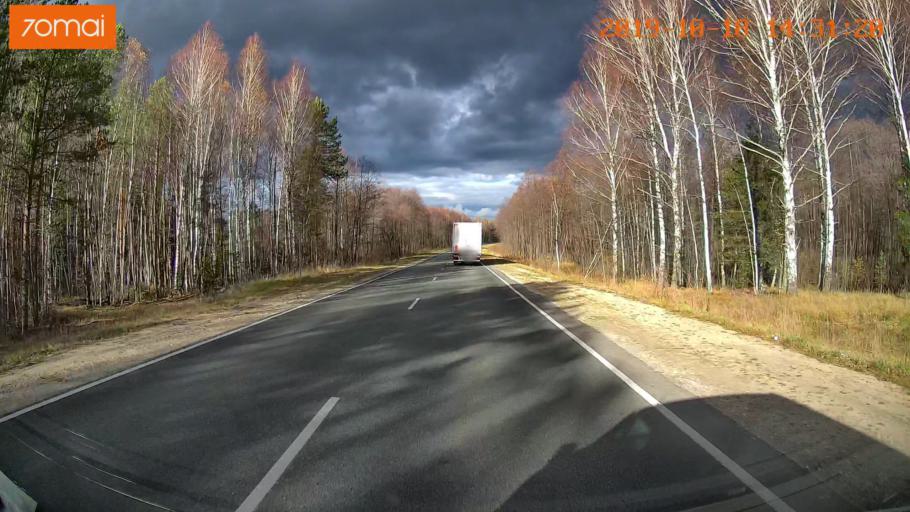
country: RU
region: Rjazan
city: Tuma
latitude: 55.1814
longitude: 40.5695
